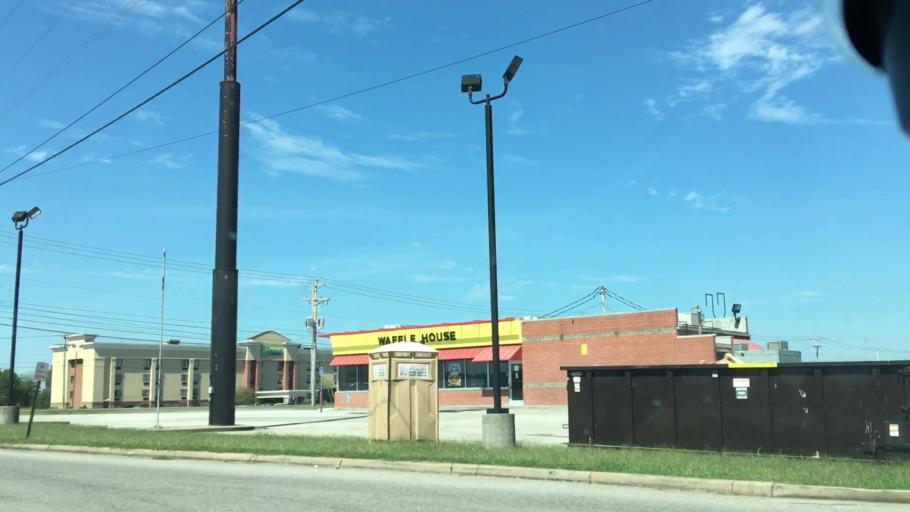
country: US
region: Kentucky
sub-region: Christian County
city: Oak Grove
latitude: 36.6930
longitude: -87.4520
